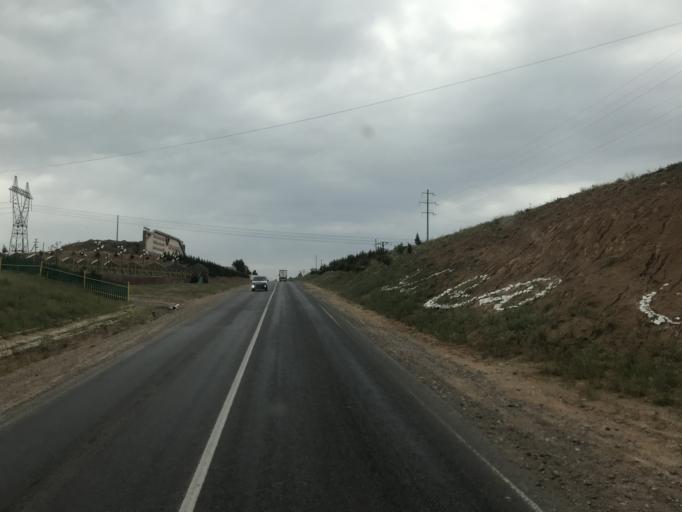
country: KZ
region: Ongtustik Qazaqstan
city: Saryaghash
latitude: 41.4807
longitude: 69.2465
